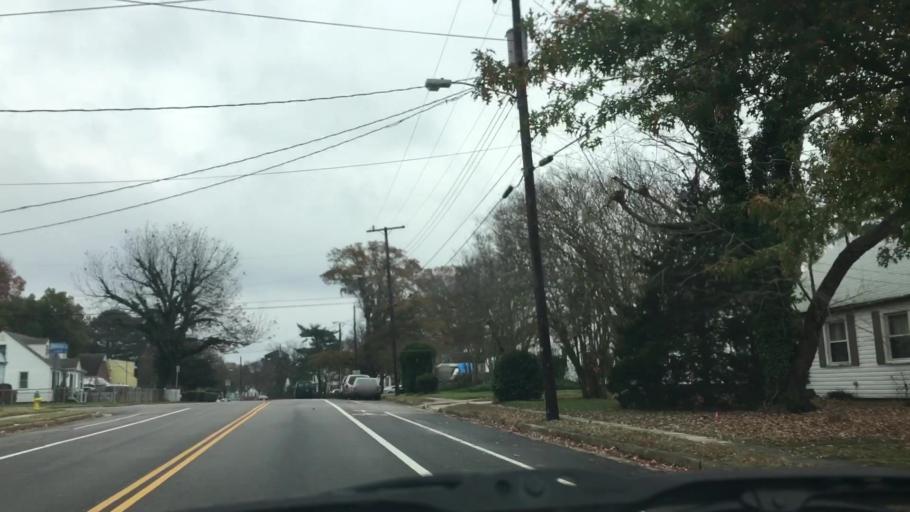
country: US
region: Virginia
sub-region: City of Norfolk
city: Norfolk
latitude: 36.8765
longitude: -76.2431
